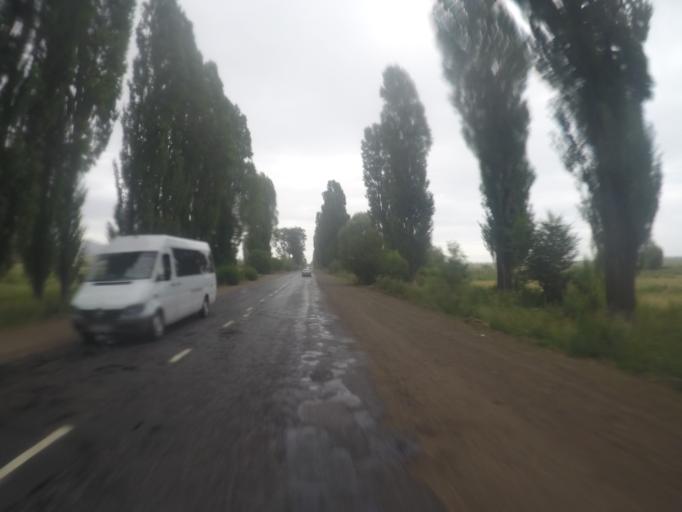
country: KG
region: Ysyk-Koel
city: Cholpon-Ata
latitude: 42.6954
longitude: 77.3935
